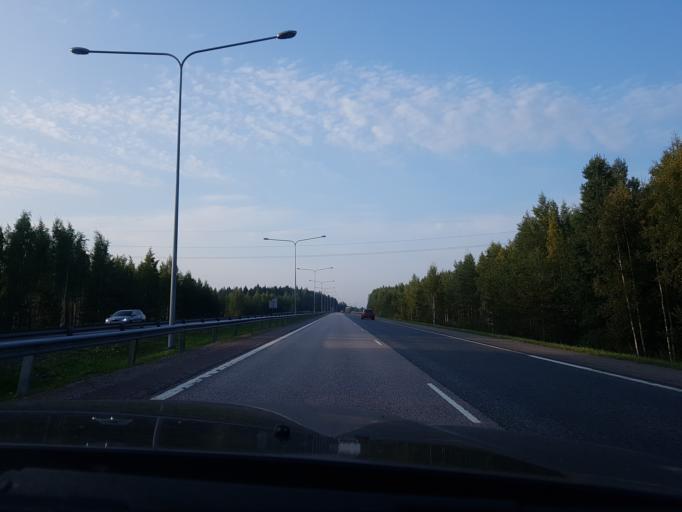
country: FI
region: Uusimaa
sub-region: Helsinki
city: Tuusula
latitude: 60.3466
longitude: 25.0010
